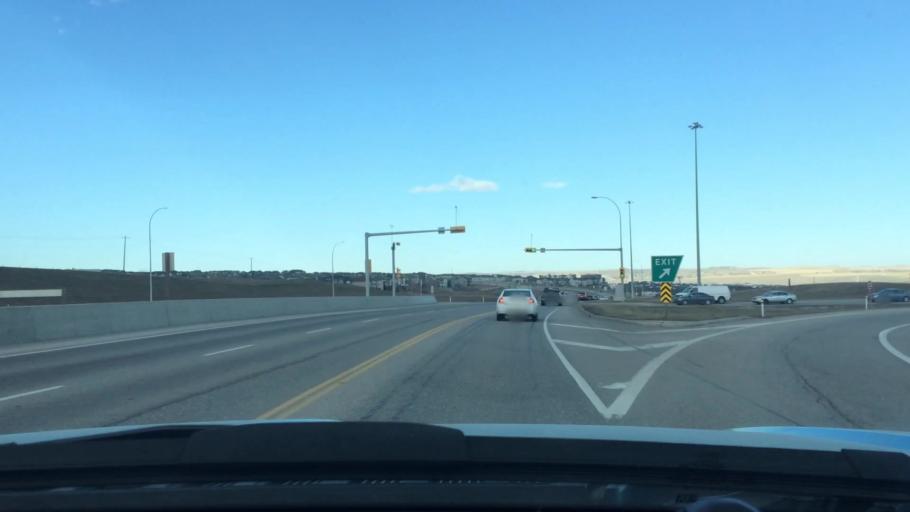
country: CA
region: Alberta
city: Calgary
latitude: 51.1533
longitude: -114.1408
